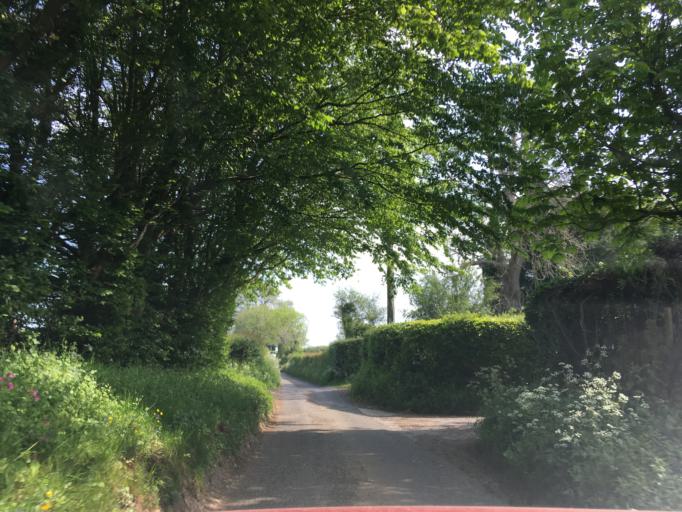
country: GB
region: England
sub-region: North Somerset
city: Dundry
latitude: 51.3944
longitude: -2.6469
